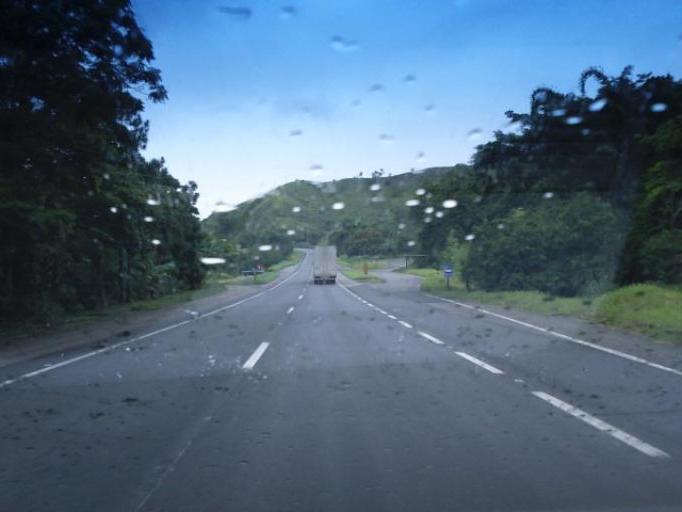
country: BR
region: Sao Paulo
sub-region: Cajati
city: Cajati
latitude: -24.8054
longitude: -48.2123
